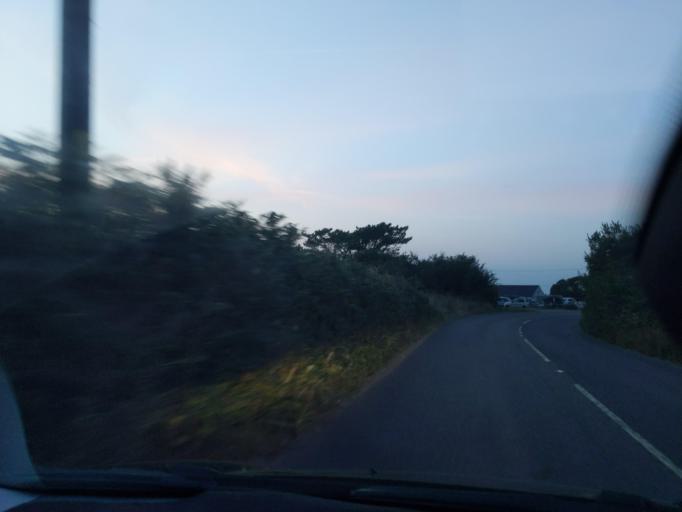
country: GB
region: England
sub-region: Cornwall
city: Camborne
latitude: 50.1850
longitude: -5.3133
